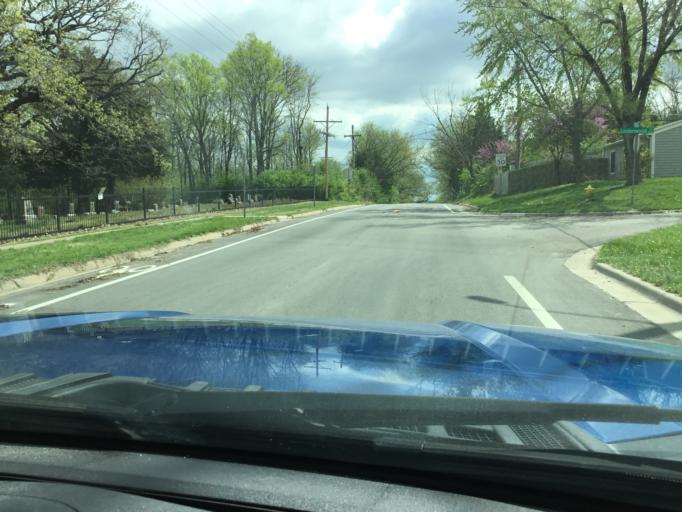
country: US
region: Kansas
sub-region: Douglas County
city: Lawrence
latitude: 38.9570
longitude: -95.2102
